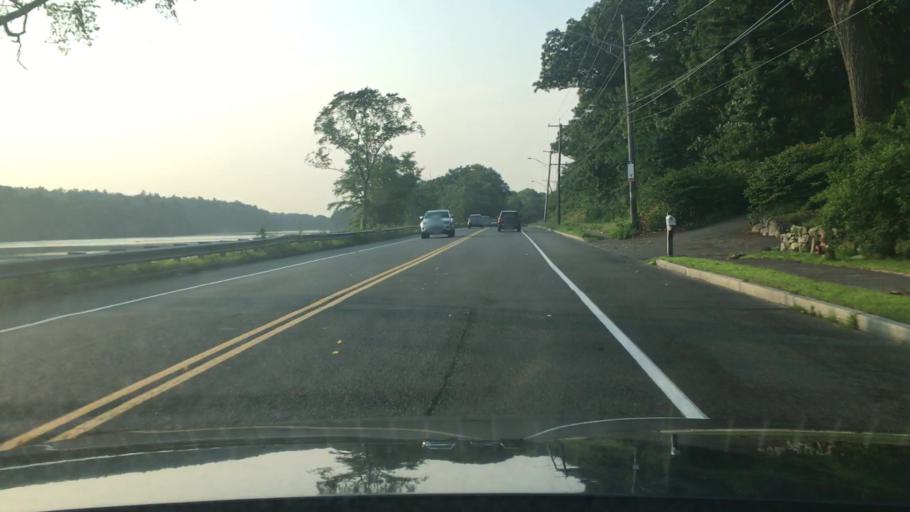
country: US
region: Massachusetts
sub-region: Essex County
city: Saugus
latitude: 42.4800
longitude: -71.0063
